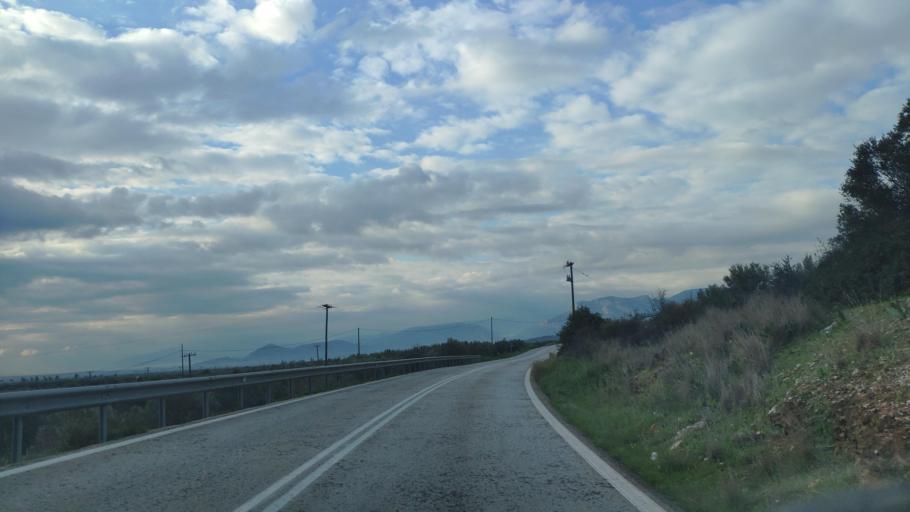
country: GR
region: Peloponnese
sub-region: Nomos Argolidos
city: Koutsopodi
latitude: 37.7330
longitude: 22.7356
